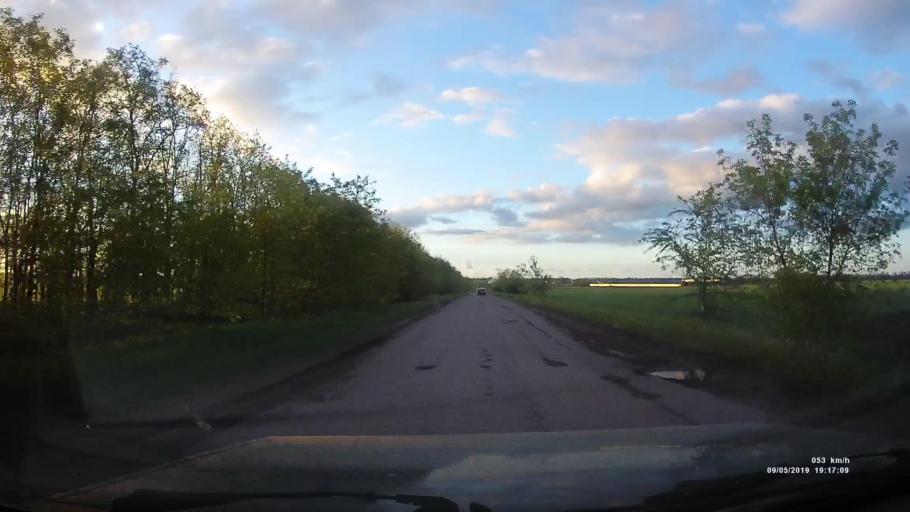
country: RU
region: Krasnodarskiy
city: Kanelovskaya
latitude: 46.7829
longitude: 39.2117
